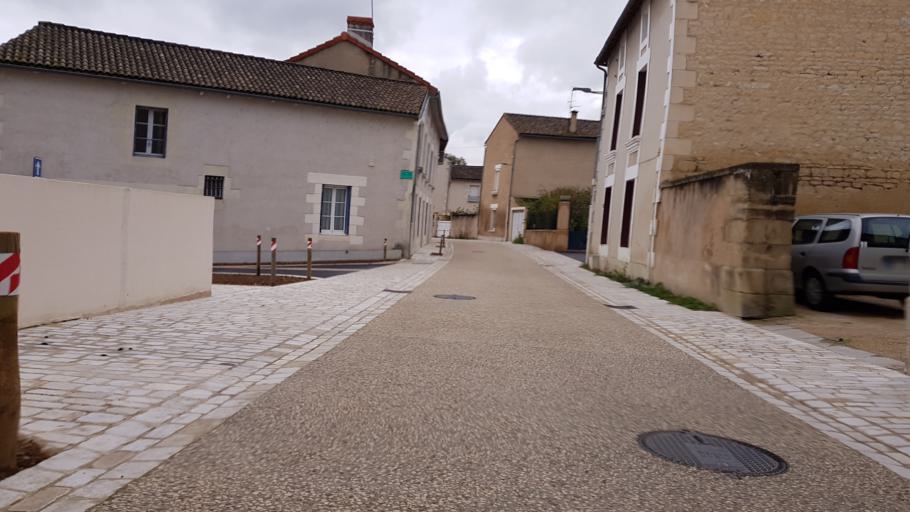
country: FR
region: Poitou-Charentes
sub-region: Departement de la Vienne
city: Chasseneuil-du-Poitou
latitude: 46.6492
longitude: 0.3733
